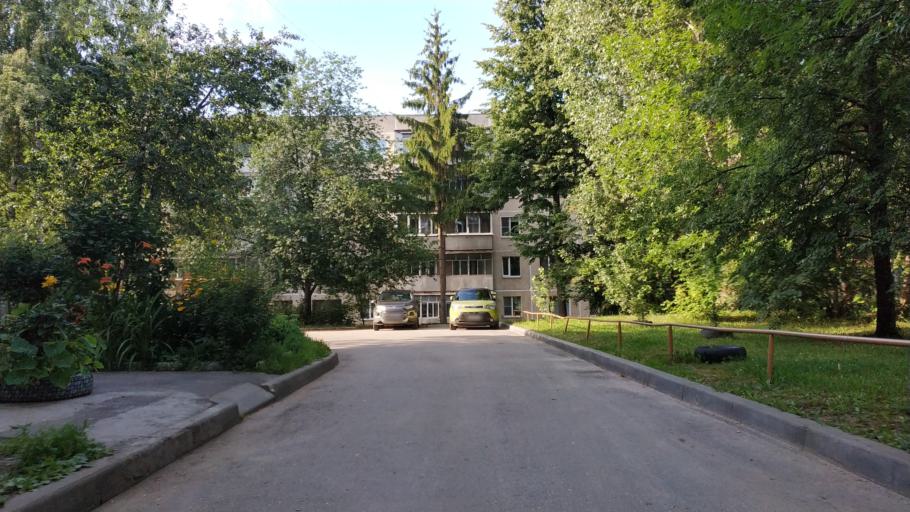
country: RU
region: Chuvashia
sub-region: Cheboksarskiy Rayon
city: Cheboksary
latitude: 56.1449
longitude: 47.1826
